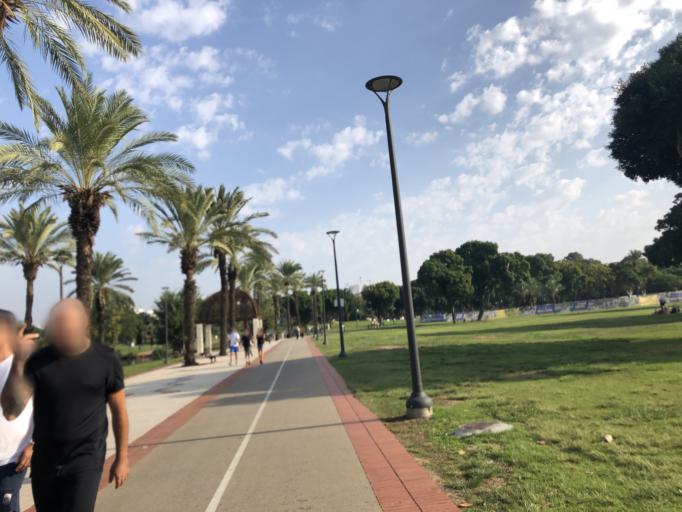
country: IL
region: Tel Aviv
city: Giv`atayim
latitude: 32.0501
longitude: 34.8252
